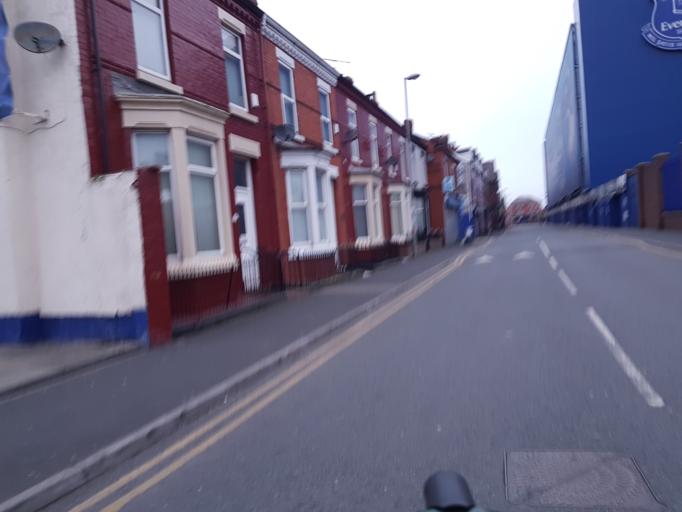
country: GB
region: England
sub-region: Liverpool
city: Liverpool
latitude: 53.4378
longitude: -2.9677
